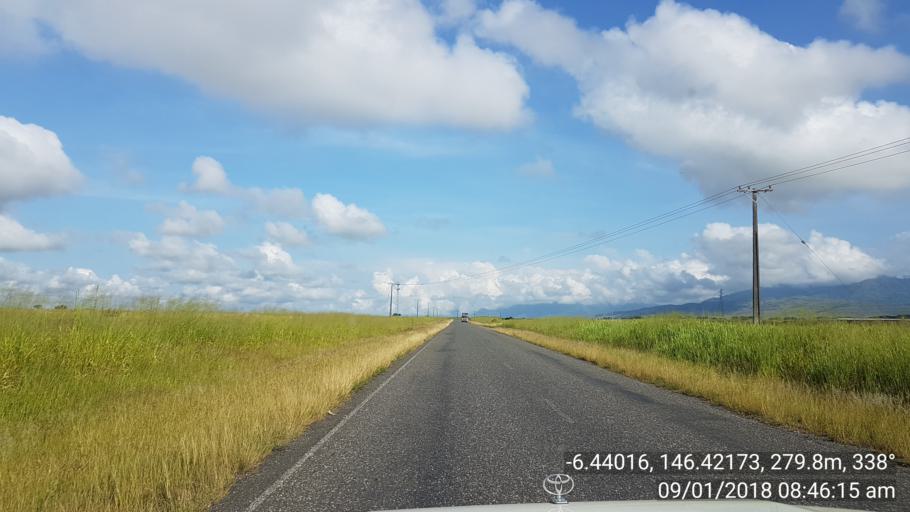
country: PG
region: Eastern Highlands
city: Kainantu
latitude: -6.4403
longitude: 146.4219
